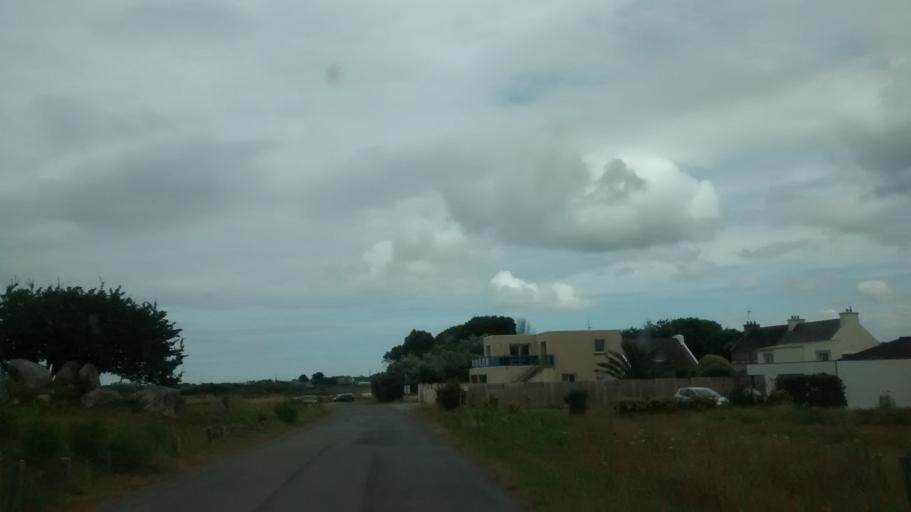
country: FR
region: Brittany
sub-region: Departement du Finistere
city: Guisseny
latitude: 48.6378
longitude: -4.4142
